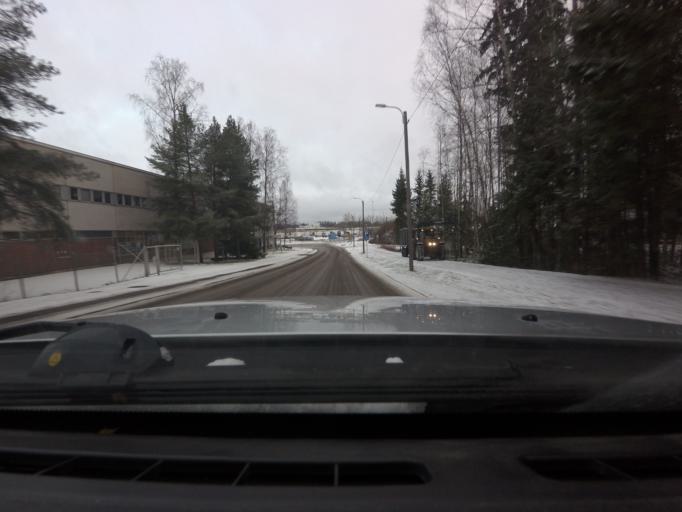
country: FI
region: Uusimaa
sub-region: Helsinki
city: Kauniainen
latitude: 60.2138
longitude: 24.7527
